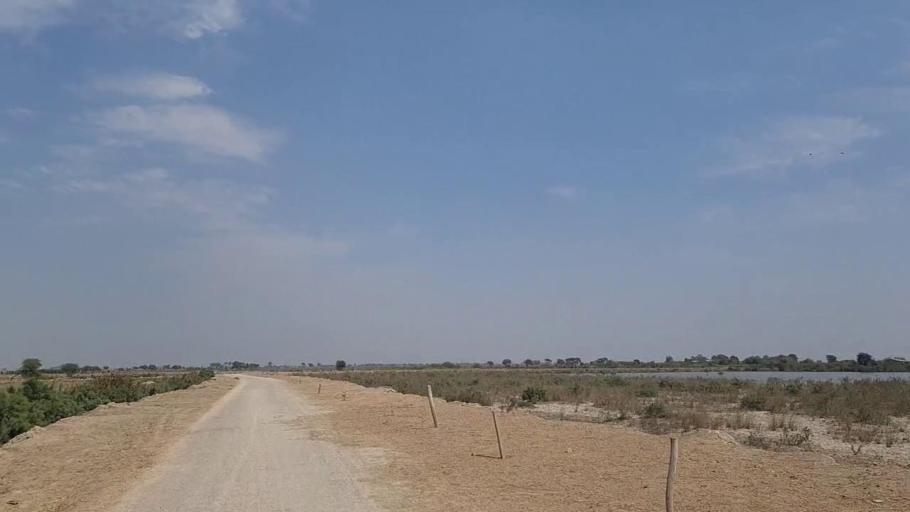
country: PK
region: Sindh
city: Mirpur Batoro
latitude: 24.5846
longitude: 68.2935
